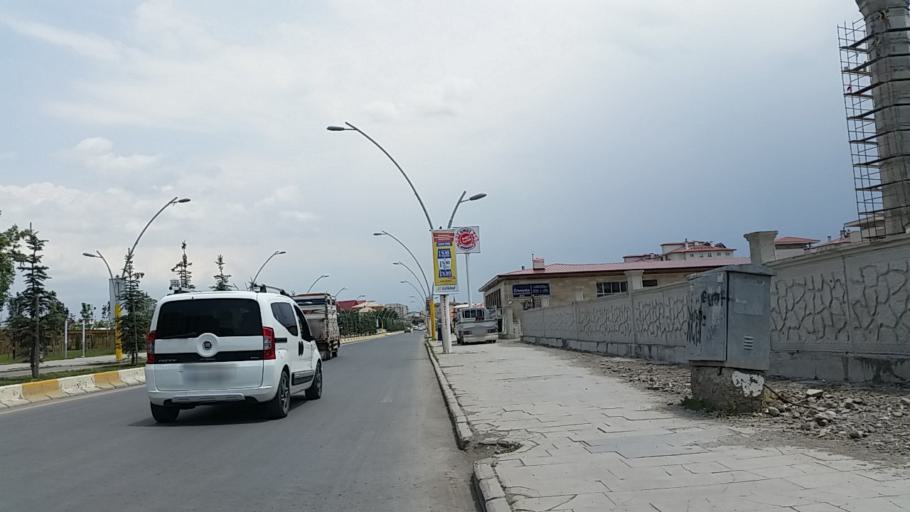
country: TR
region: Agri
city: Agri
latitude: 39.7188
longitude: 43.0341
